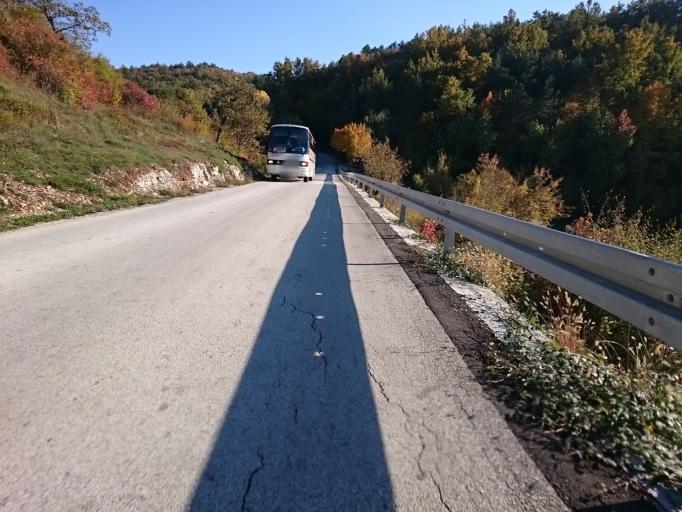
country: HR
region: Istarska
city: Buje
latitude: 45.3910
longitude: 13.7200
